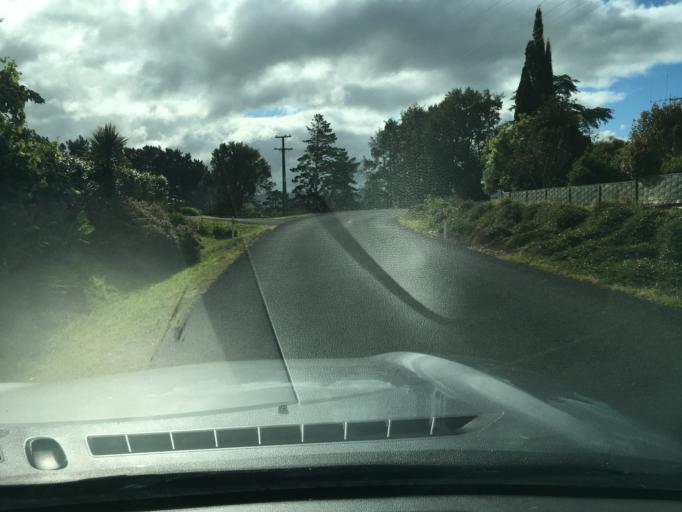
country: NZ
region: Waikato
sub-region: Hamilton City
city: Hamilton
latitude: -37.8248
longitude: 175.1759
